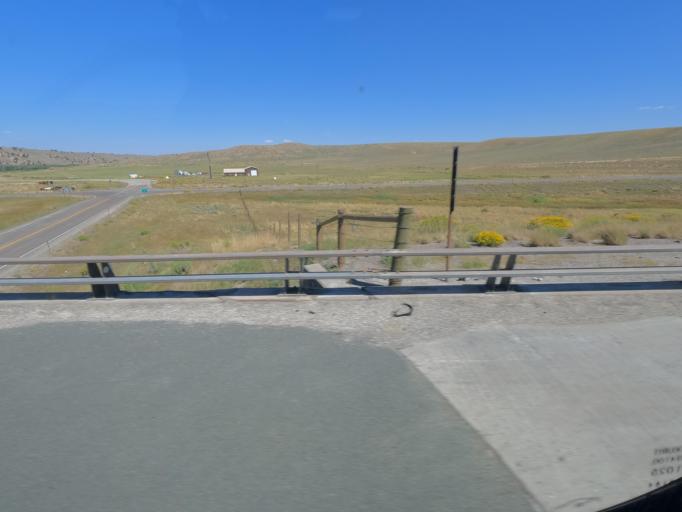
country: US
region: Wyoming
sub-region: Carbon County
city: Saratoga
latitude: 41.6944
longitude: -106.3829
